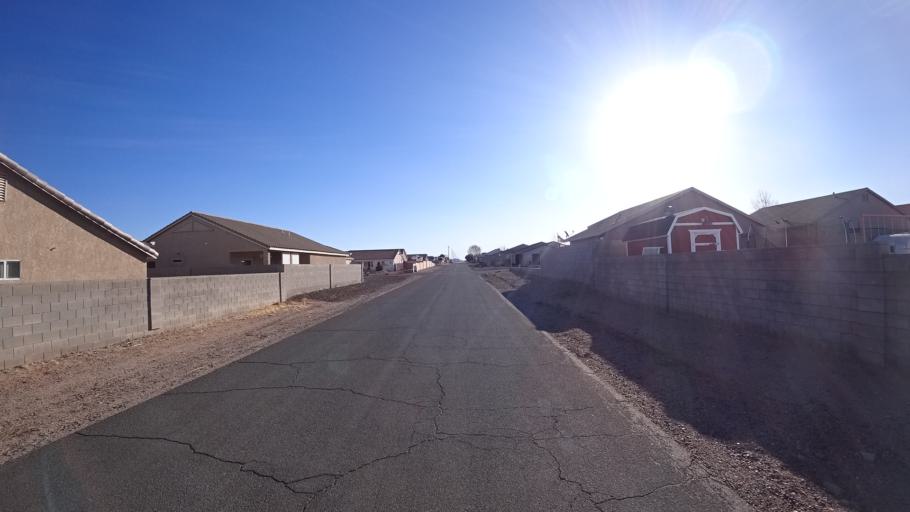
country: US
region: Arizona
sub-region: Mohave County
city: Kingman
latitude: 35.2121
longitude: -114.0066
